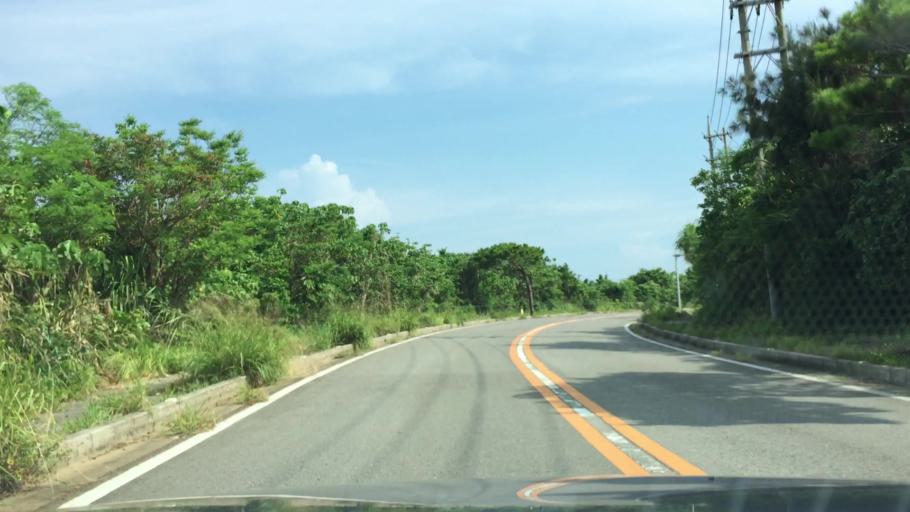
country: JP
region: Okinawa
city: Ishigaki
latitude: 24.4909
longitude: 124.2799
